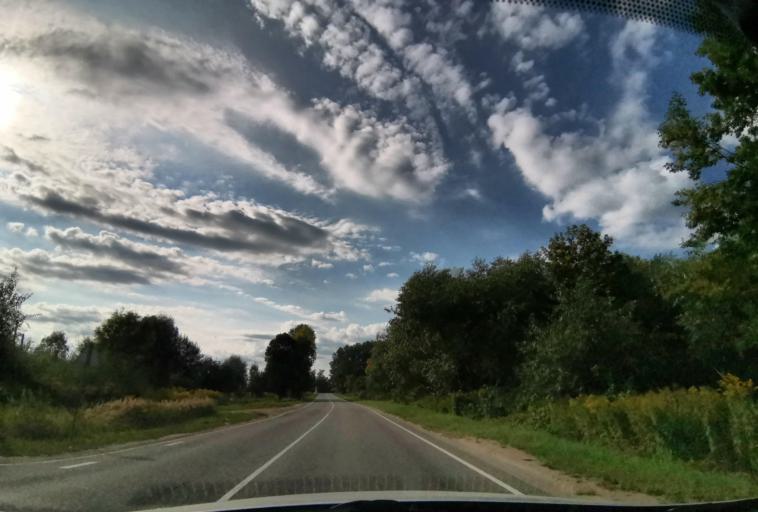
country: RU
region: Kaliningrad
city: Neman
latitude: 55.0203
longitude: 22.0795
